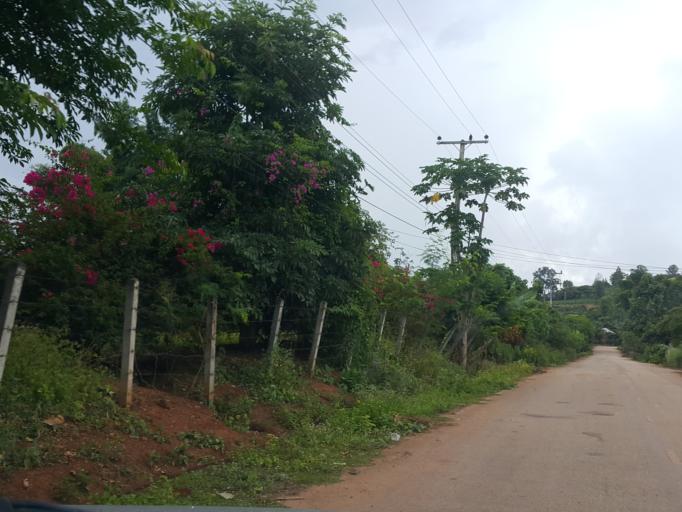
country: TH
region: Chiang Mai
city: Phrao
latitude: 19.3310
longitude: 99.1490
